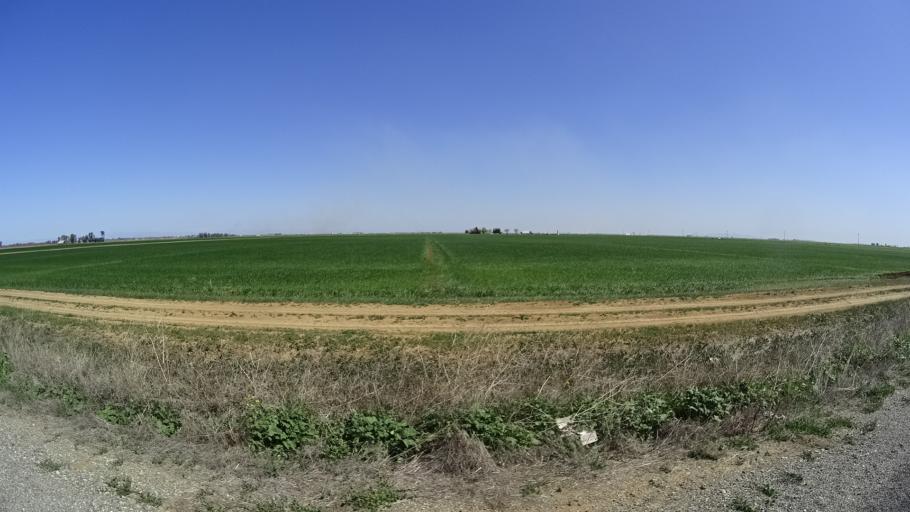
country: US
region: California
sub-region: Glenn County
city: Willows
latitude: 39.4883
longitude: -122.2490
